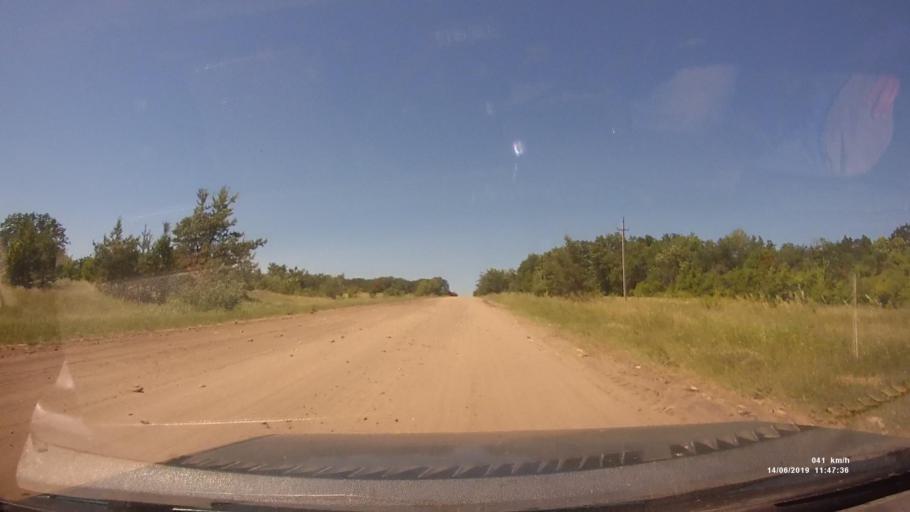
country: RU
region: Rostov
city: Kazanskaya
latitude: 49.8515
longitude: 41.2941
